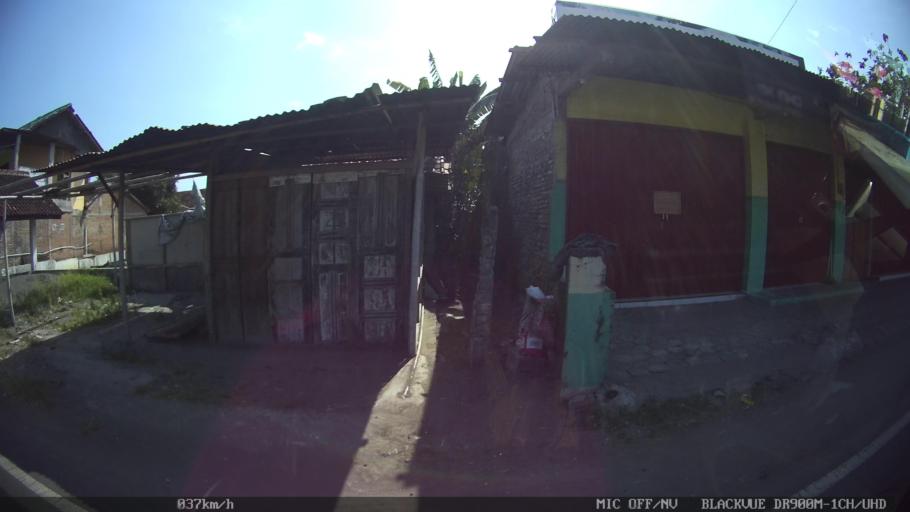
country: ID
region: Daerah Istimewa Yogyakarta
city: Sewon
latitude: -7.9074
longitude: 110.3832
